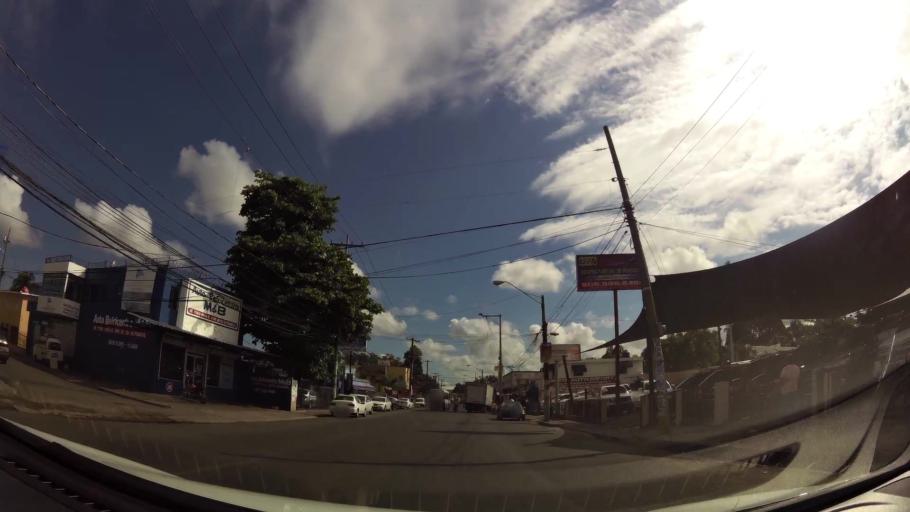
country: DO
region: Santo Domingo
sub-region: Santo Domingo
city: Santo Domingo Este
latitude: 18.4956
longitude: -69.8619
